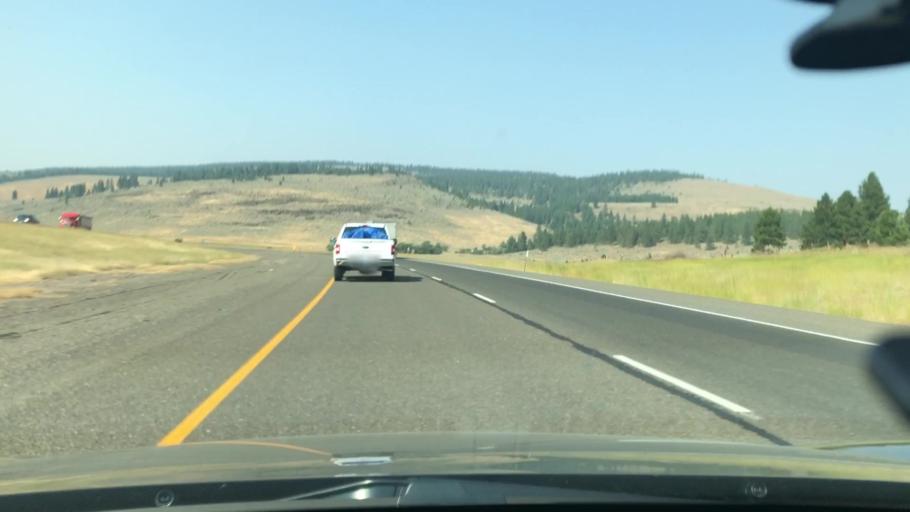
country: US
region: Oregon
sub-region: Union County
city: Union
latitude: 45.1579
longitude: -117.9660
